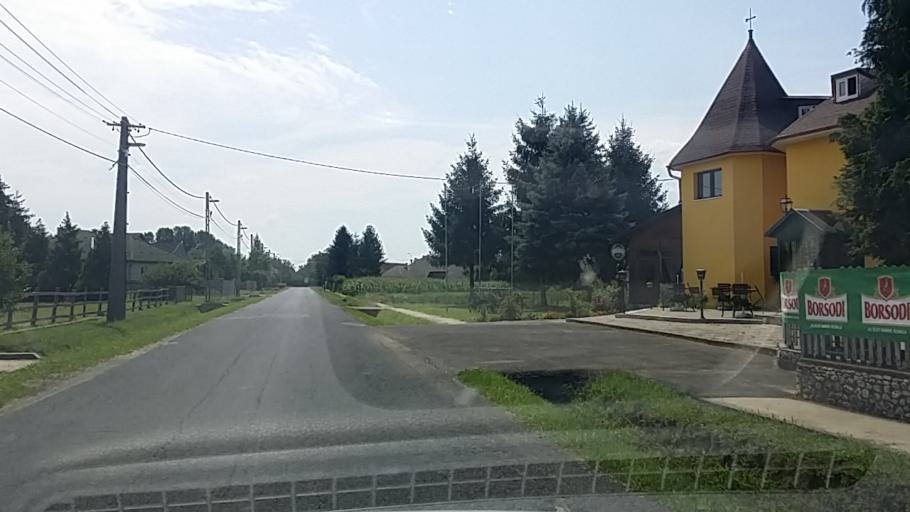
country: HU
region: Zala
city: Letenye
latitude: 46.4260
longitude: 16.7338
